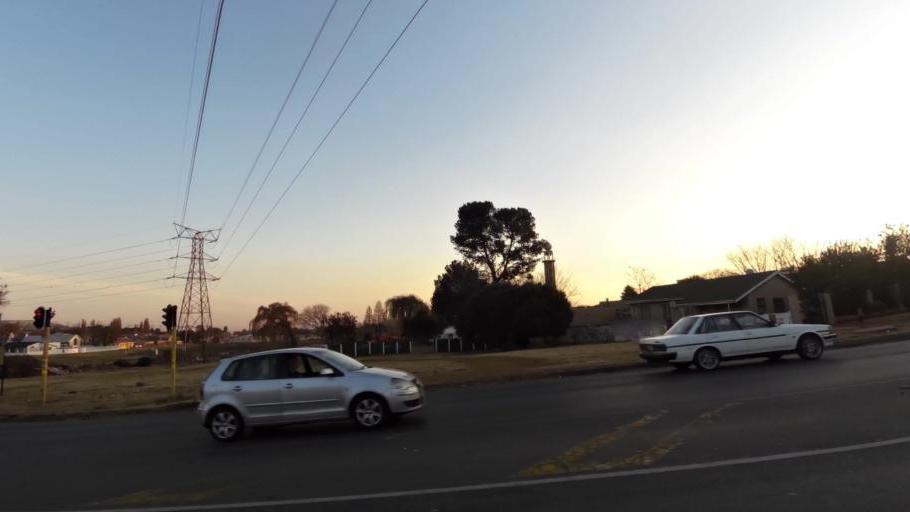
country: ZA
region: Gauteng
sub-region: City of Johannesburg Metropolitan Municipality
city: Johannesburg
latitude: -26.1901
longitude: 27.9580
